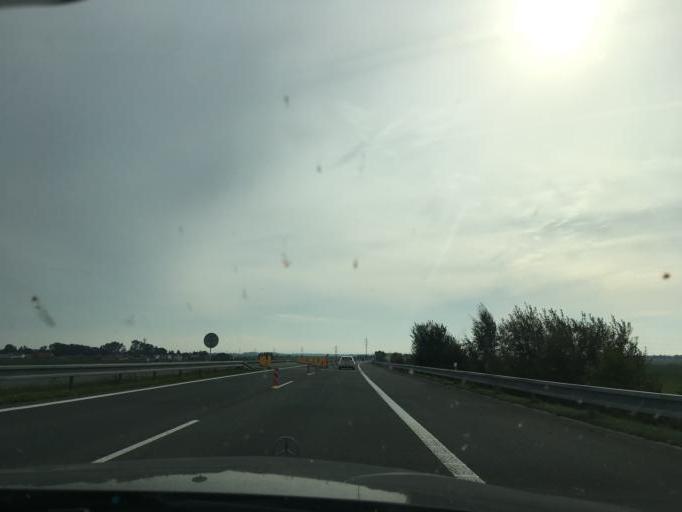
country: CZ
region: Pardubicky
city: Opatovice nad Labem
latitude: 50.1668
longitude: 15.7576
